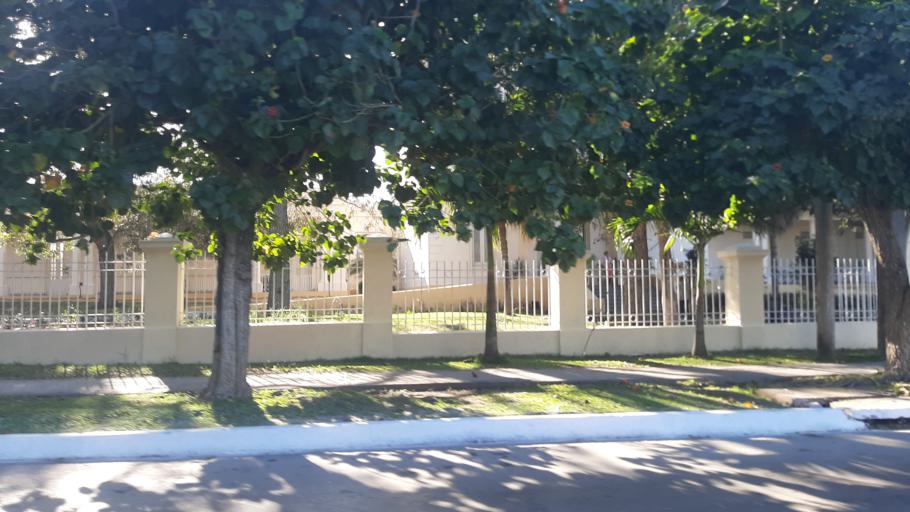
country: CU
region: Villa Clara
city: Santa Clara
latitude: 22.4108
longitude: -79.9595
